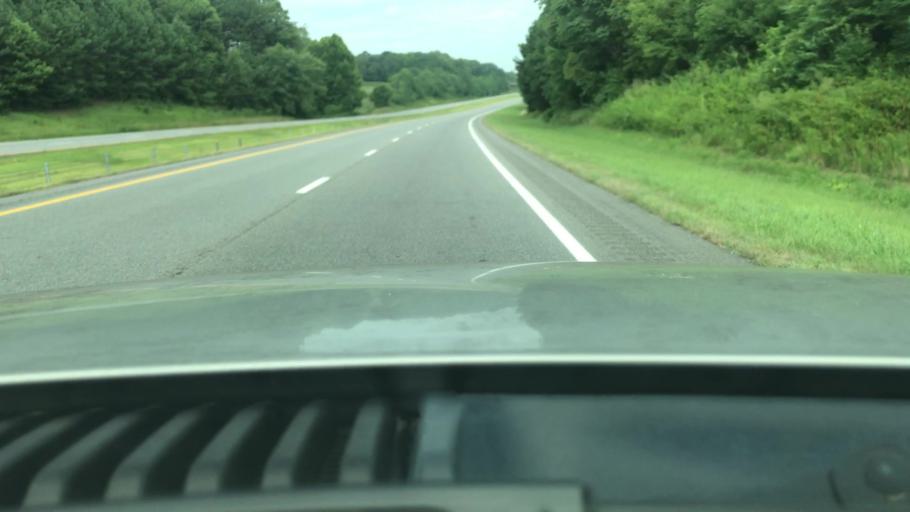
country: US
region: North Carolina
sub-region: Surry County
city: Elkin
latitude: 36.1602
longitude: -80.9667
